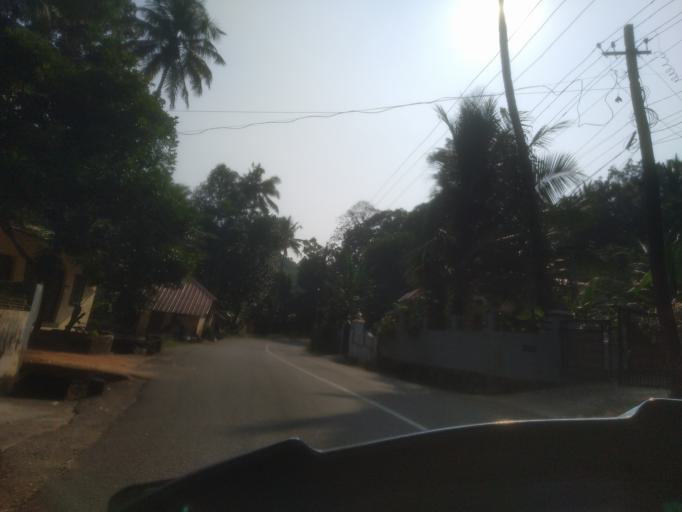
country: IN
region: Kerala
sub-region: Ernakulam
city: Piravam
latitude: 9.8704
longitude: 76.5448
